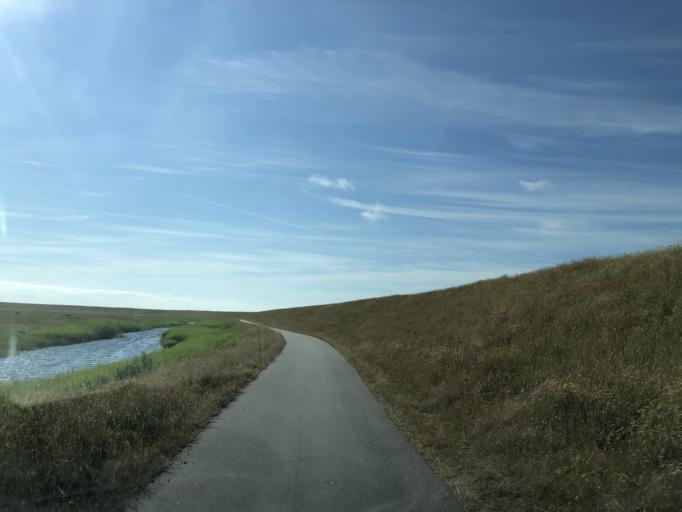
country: DK
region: South Denmark
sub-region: Esbjerg Kommune
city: Tjaereborg
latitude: 55.2926
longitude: 8.5668
